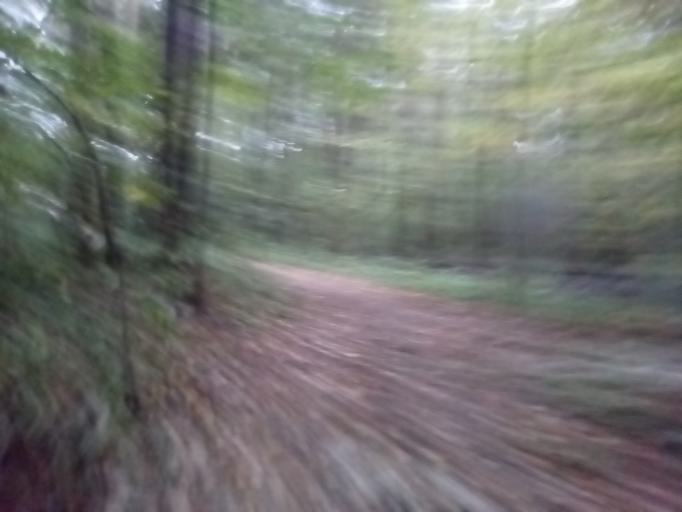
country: RU
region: Moskovskaya
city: Kokoshkino
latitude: 55.6194
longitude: 37.1648
